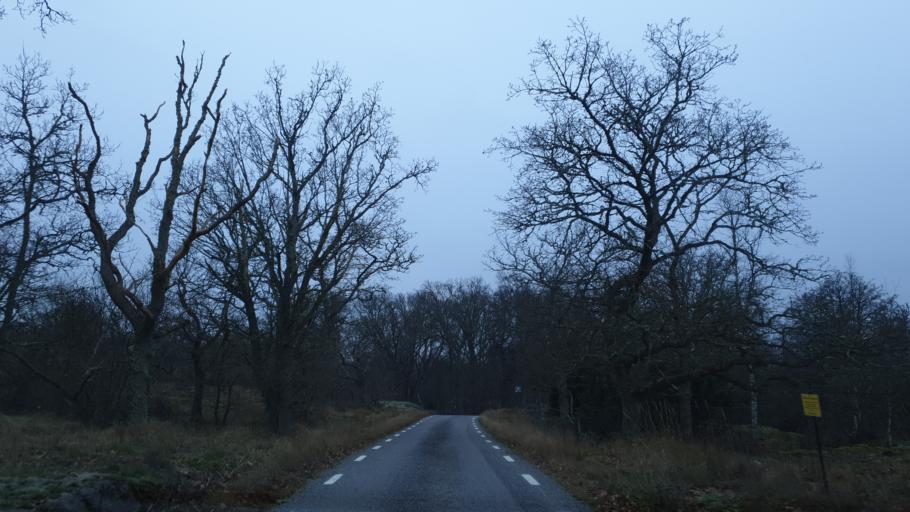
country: SE
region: Blekinge
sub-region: Karlskrona Kommun
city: Karlskrona
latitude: 56.1051
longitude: 15.6060
